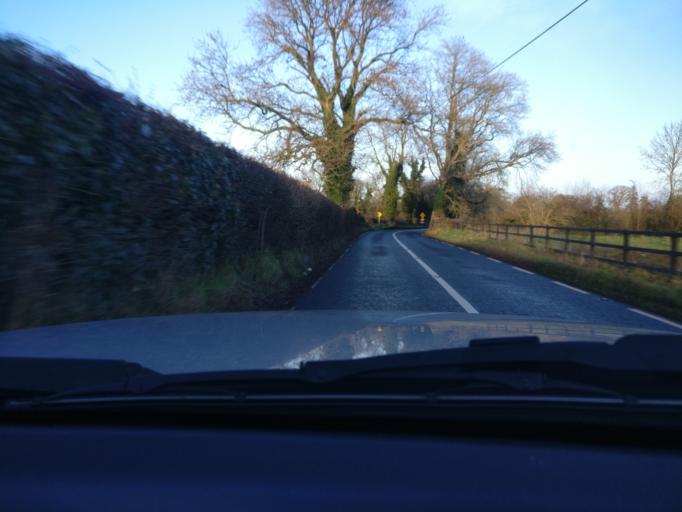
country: IE
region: Ulster
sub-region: An Cabhan
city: Kingscourt
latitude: 53.7952
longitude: -6.7171
